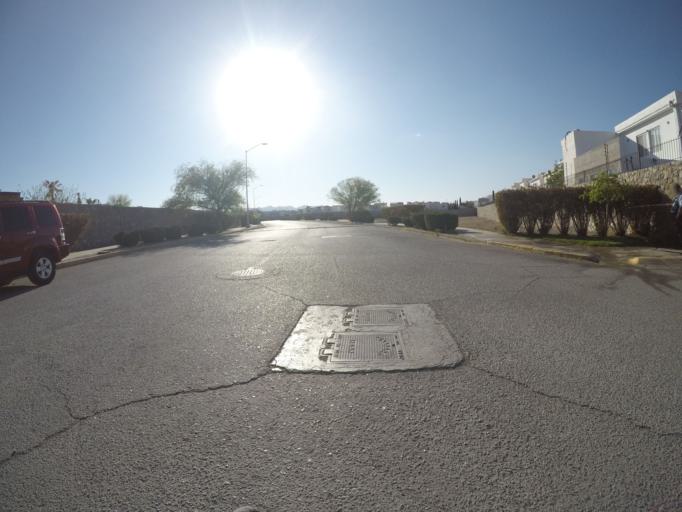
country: MX
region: Chihuahua
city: Ciudad Juarez
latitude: 31.7032
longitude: -106.3941
